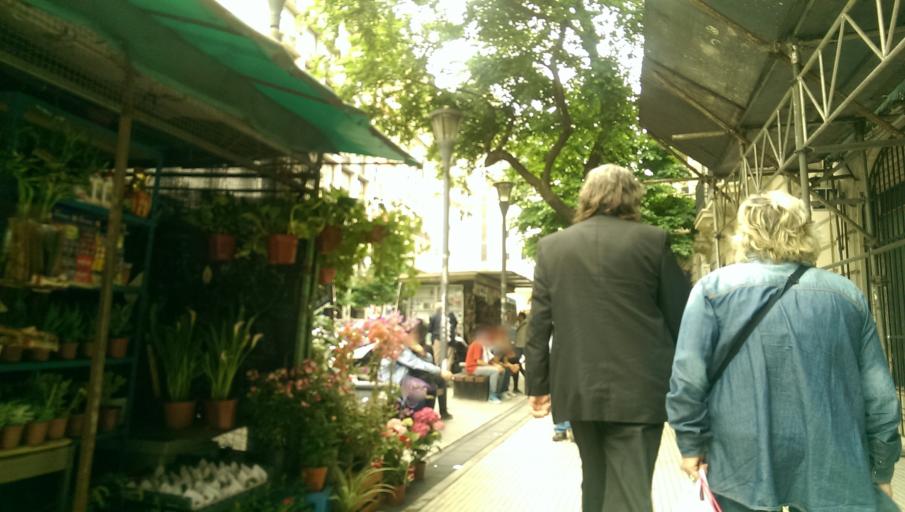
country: AR
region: Buenos Aires F.D.
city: Buenos Aires
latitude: -34.6016
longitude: -58.3867
